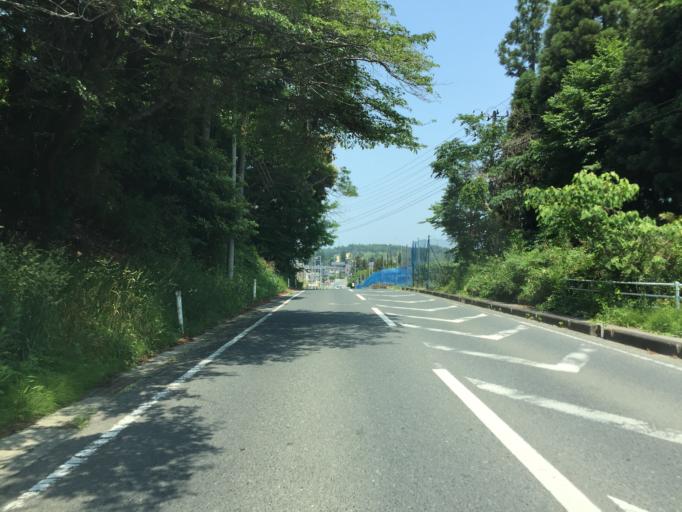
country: JP
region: Miyagi
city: Marumori
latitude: 37.8262
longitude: 140.8959
